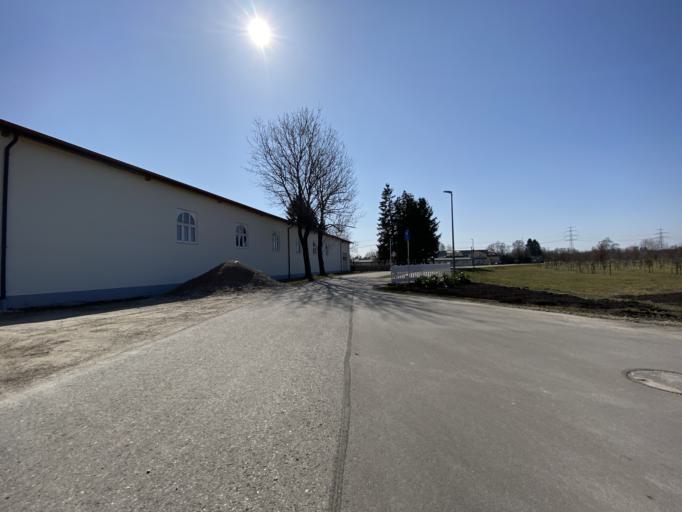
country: DE
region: Bavaria
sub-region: Upper Bavaria
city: Unterfoehring
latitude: 48.1844
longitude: 11.6563
